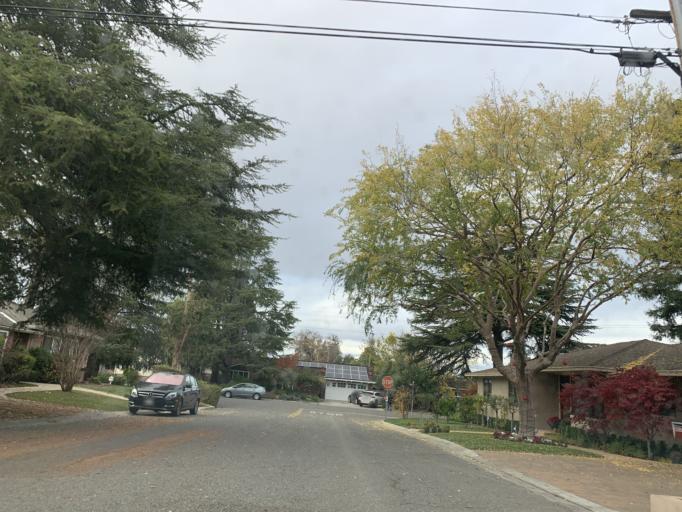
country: US
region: California
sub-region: Santa Clara County
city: Monte Sereno
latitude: 37.2677
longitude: -121.9918
